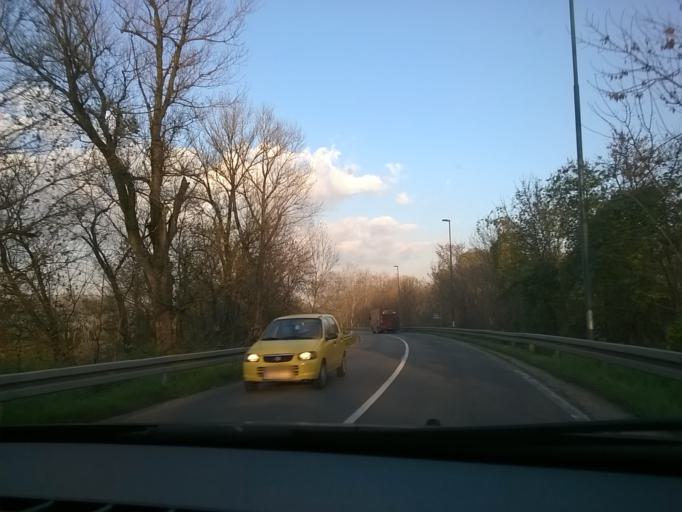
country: RS
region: Autonomna Pokrajina Vojvodina
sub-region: Juznobanatski Okrug
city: Pancevo
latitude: 44.8684
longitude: 20.6275
